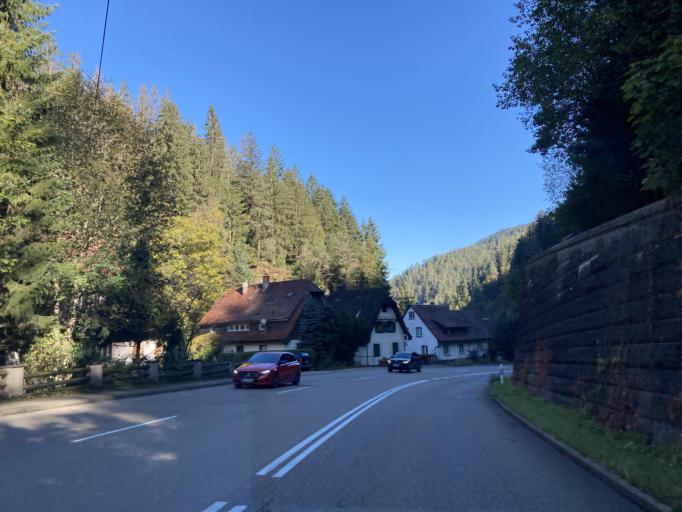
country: DE
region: Baden-Wuerttemberg
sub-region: Freiburg Region
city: Triberg im Schwarzwald
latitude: 48.1541
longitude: 8.2395
